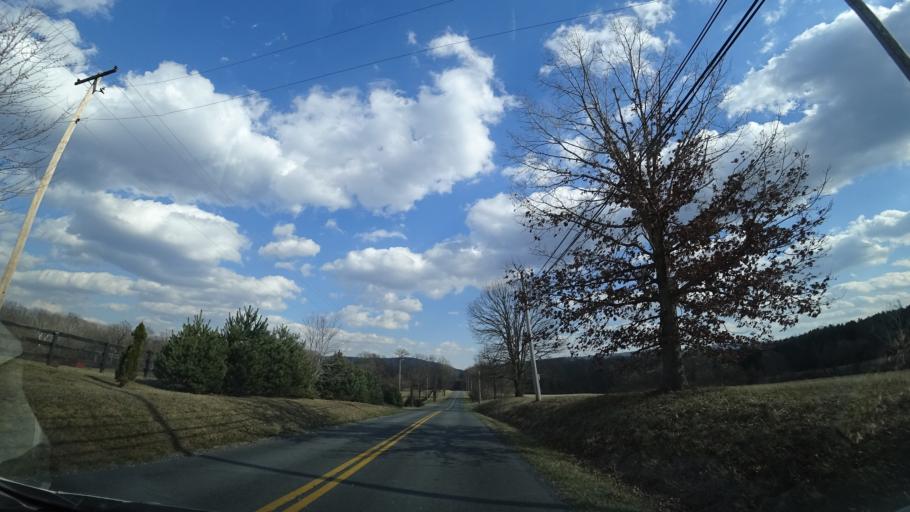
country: US
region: Virginia
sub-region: Warren County
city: Shenandoah Farms
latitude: 39.0539
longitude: -78.0166
